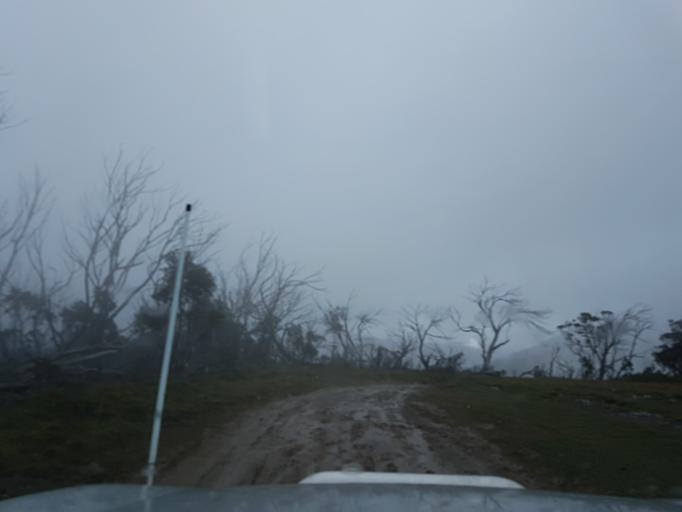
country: AU
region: Victoria
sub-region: Alpine
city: Mount Beauty
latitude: -37.0847
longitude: 147.1192
